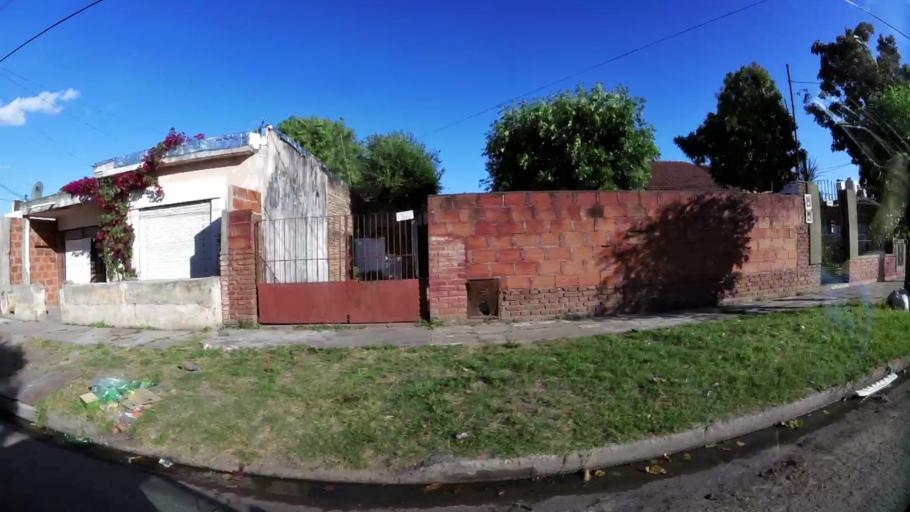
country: AR
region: Buenos Aires
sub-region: Partido de Moron
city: Moron
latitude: -34.6855
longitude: -58.6309
